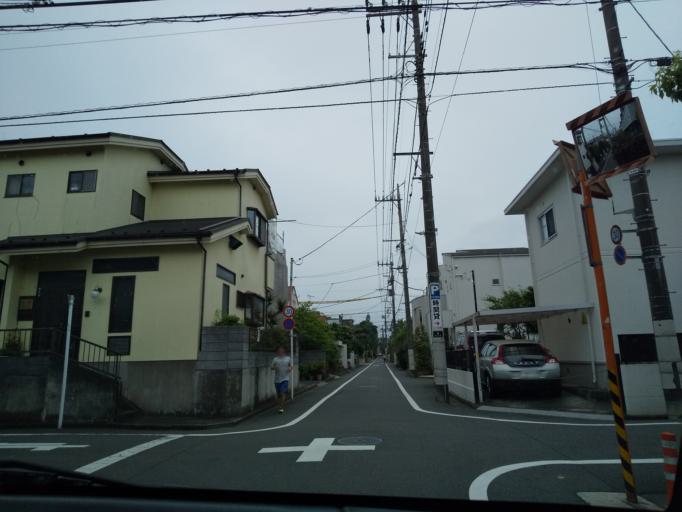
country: JP
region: Tokyo
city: Kokubunji
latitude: 35.6901
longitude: 139.4501
